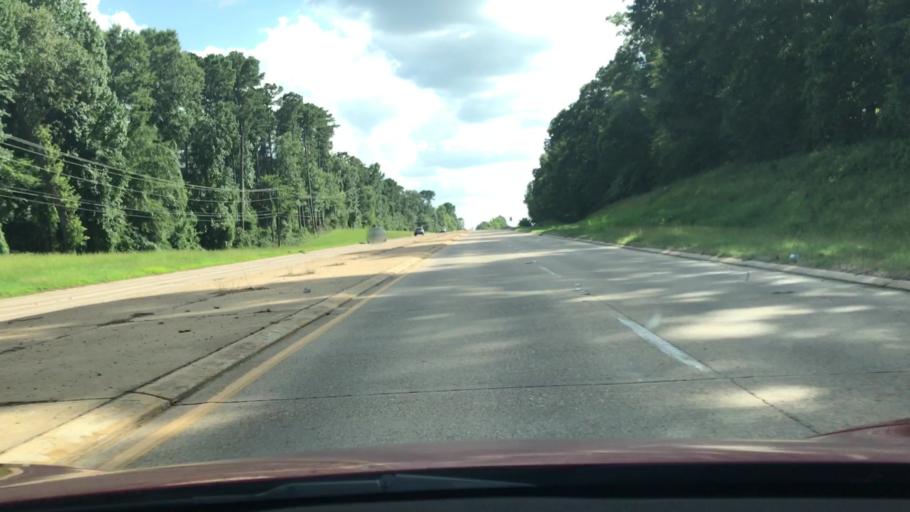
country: US
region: Louisiana
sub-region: Bossier Parish
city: Bossier City
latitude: 32.4059
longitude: -93.7295
